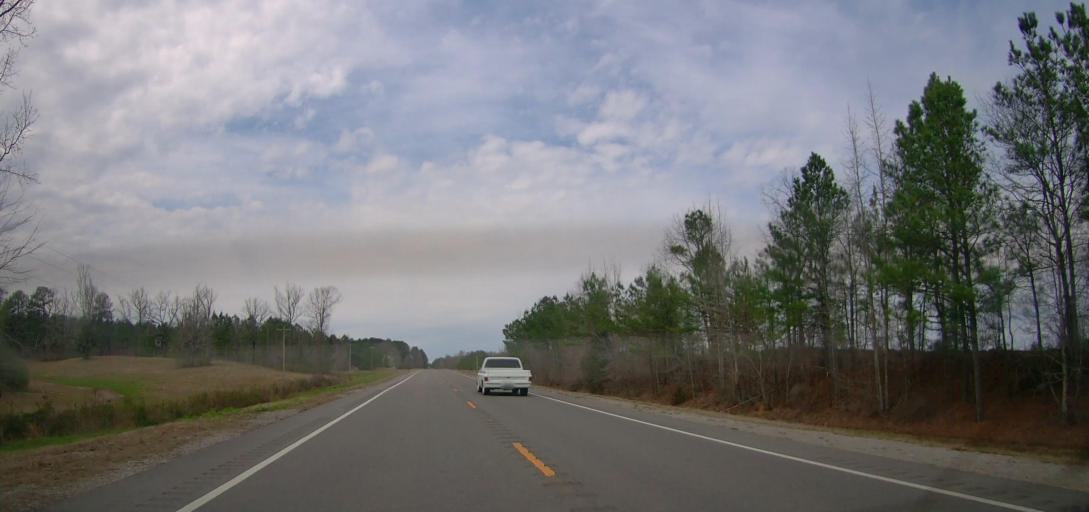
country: US
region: Alabama
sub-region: Marion County
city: Guin
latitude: 34.0028
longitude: -87.9323
